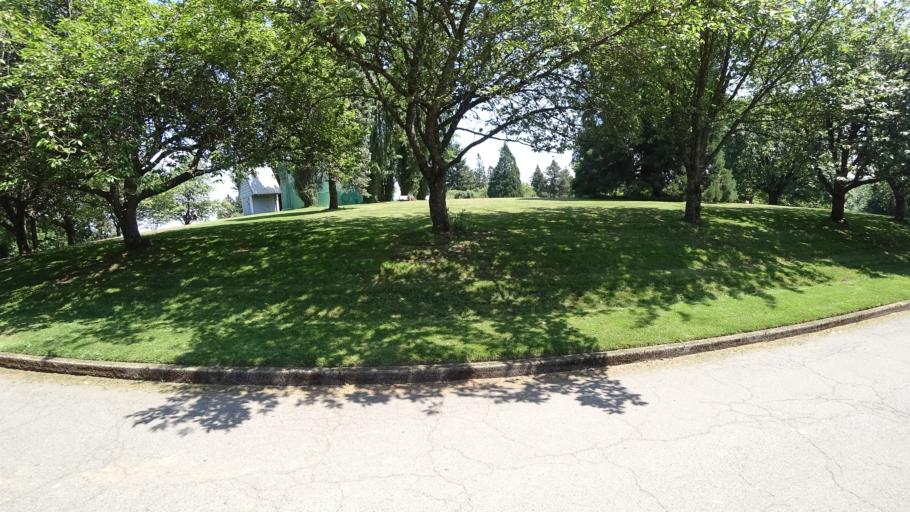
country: US
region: Oregon
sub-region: Multnomah County
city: Portland
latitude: 45.4990
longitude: -122.7088
